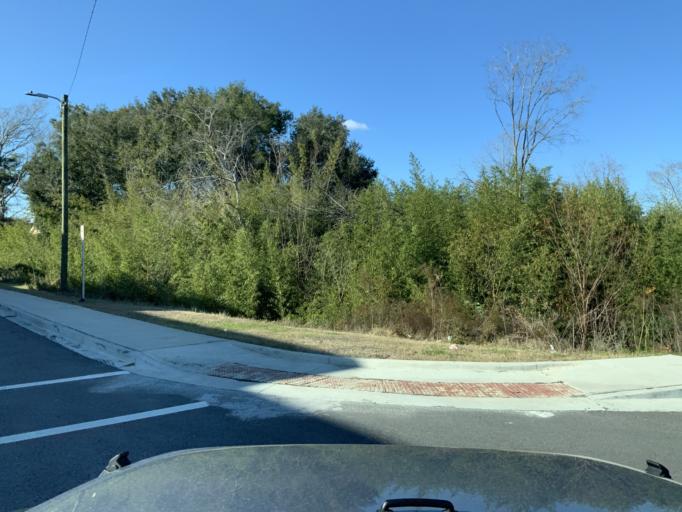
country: US
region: Georgia
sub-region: Chatham County
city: Savannah
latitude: 32.0735
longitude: -81.0811
